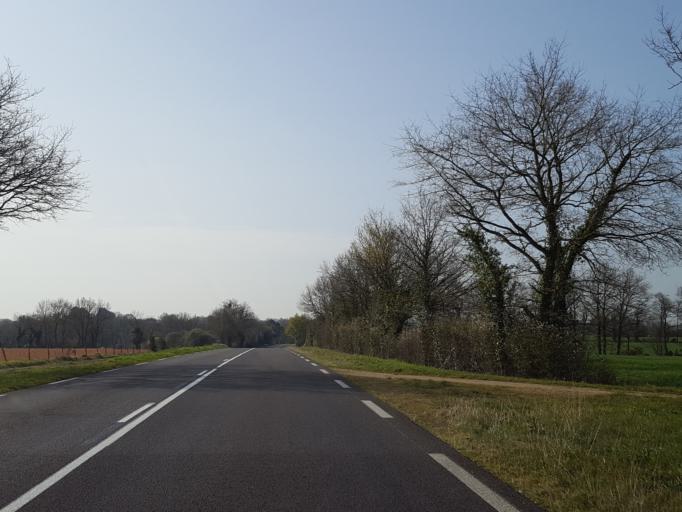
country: FR
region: Pays de la Loire
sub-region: Departement de la Vendee
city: Les Lucs-sur-Boulogne
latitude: 46.8675
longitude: -1.4990
